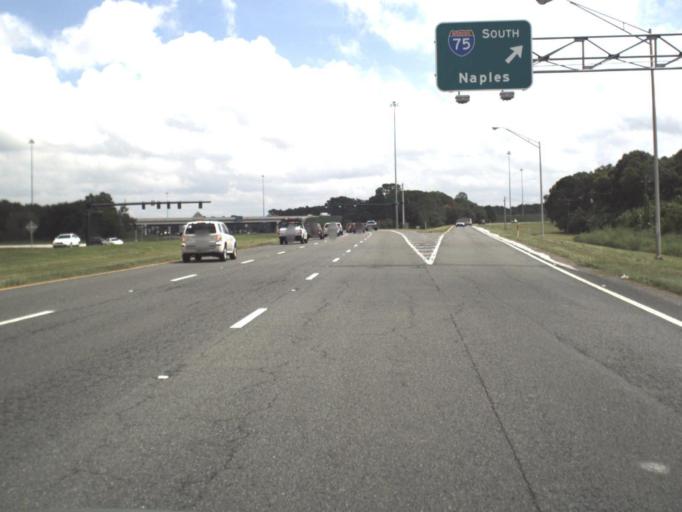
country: US
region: Florida
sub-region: Manatee County
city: Ellenton
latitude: 27.4915
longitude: -82.4768
